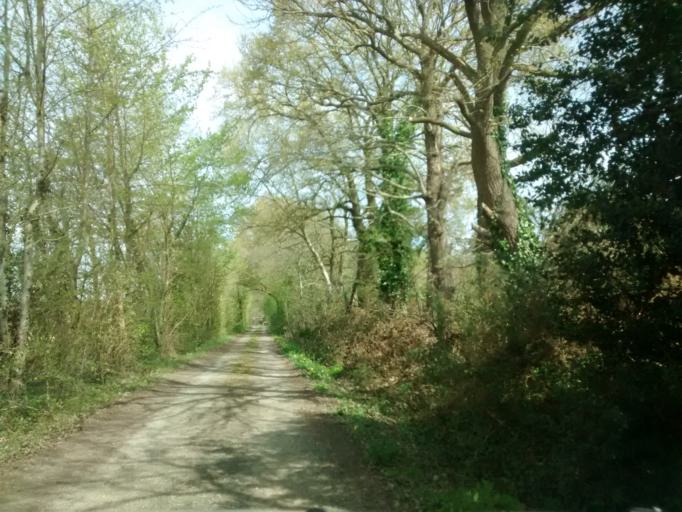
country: FR
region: Brittany
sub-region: Departement d'Ille-et-Vilaine
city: Fouillard
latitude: 48.1677
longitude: -1.5963
